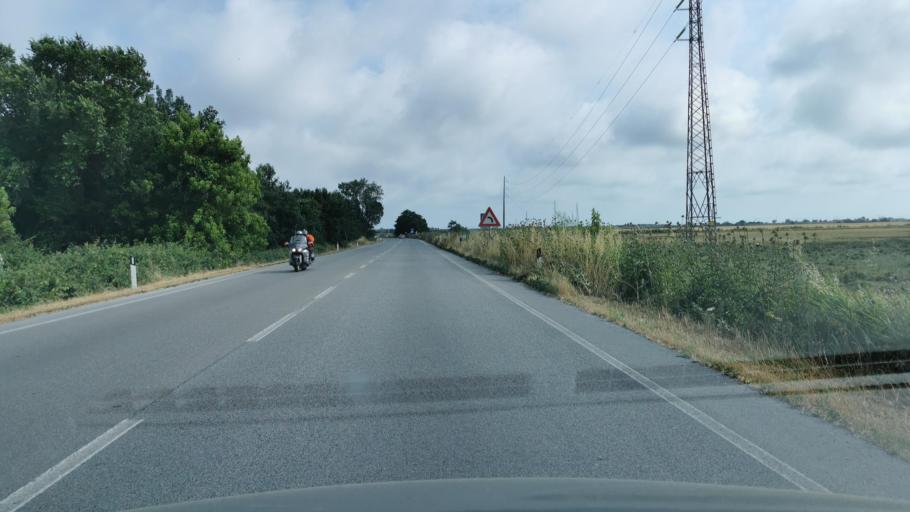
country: IT
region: Emilia-Romagna
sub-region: Provincia di Ravenna
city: Marina Romea
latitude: 44.5713
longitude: 12.2534
